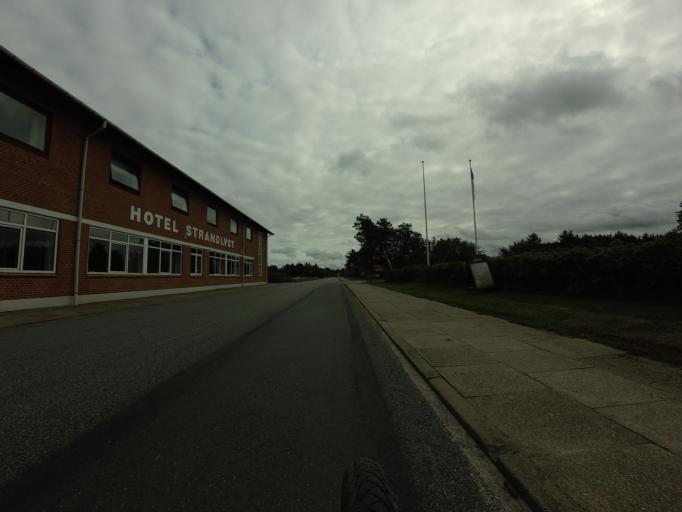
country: DK
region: North Denmark
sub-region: Hjorring Kommune
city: Hirtshals
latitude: 57.5554
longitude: 9.9324
